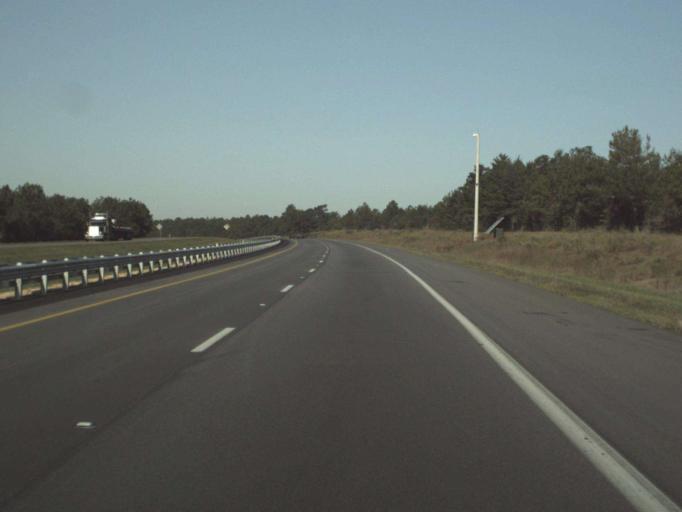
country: US
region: Florida
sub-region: Walton County
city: DeFuniak Springs
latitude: 30.7207
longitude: -86.1826
